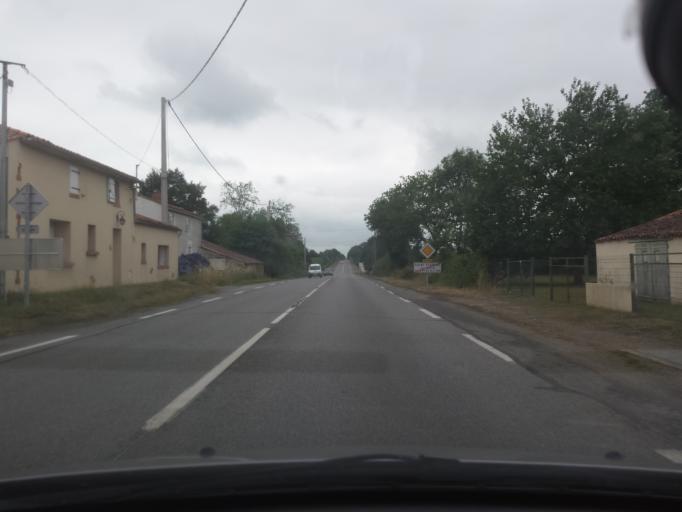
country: FR
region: Pays de la Loire
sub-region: Departement de la Vendee
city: Saint-Florent-des-Bois
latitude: 46.6005
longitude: -1.3280
